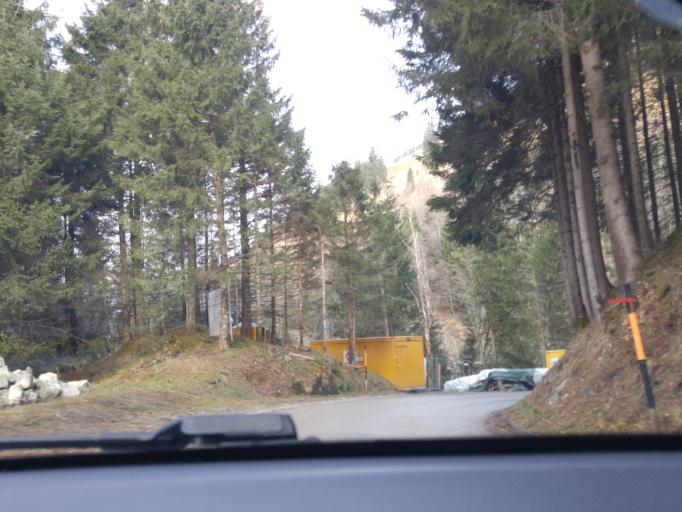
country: AT
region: Salzburg
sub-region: Politischer Bezirk Zell am See
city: Niedernsill
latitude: 47.1973
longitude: 12.6117
